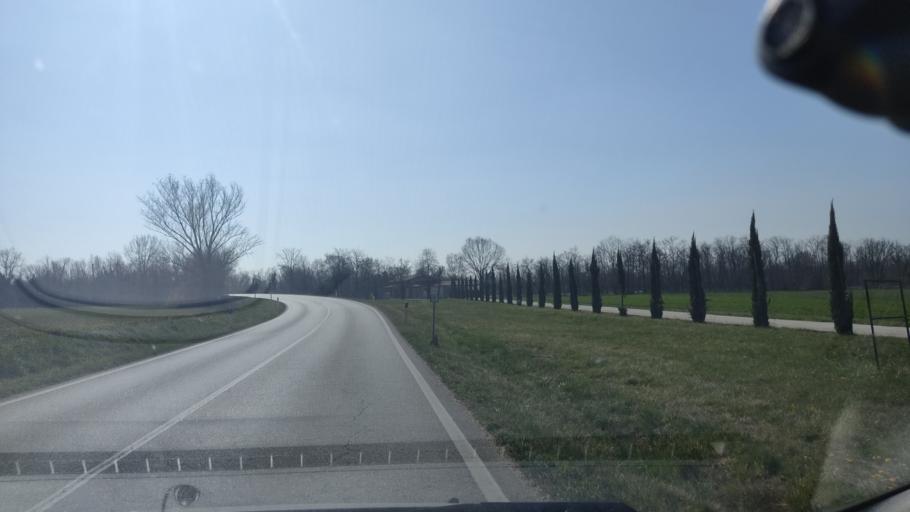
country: IT
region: Friuli Venezia Giulia
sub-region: Provincia di Pordenone
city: Budoia
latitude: 46.0324
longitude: 12.5517
